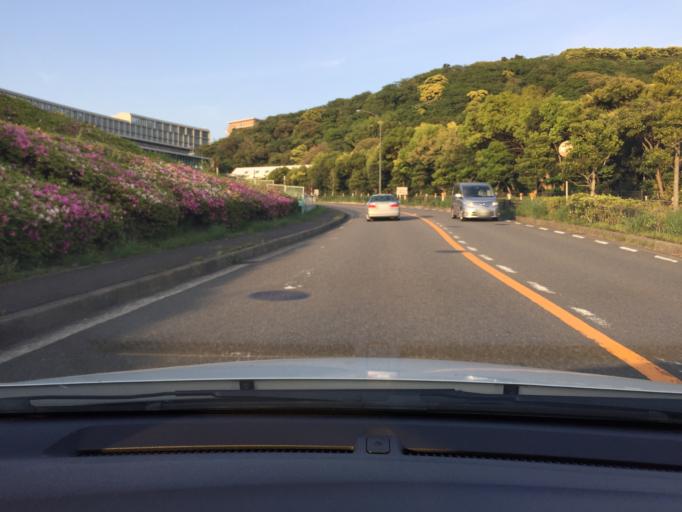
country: JP
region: Kanagawa
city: Hayama
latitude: 35.2531
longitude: 139.6071
